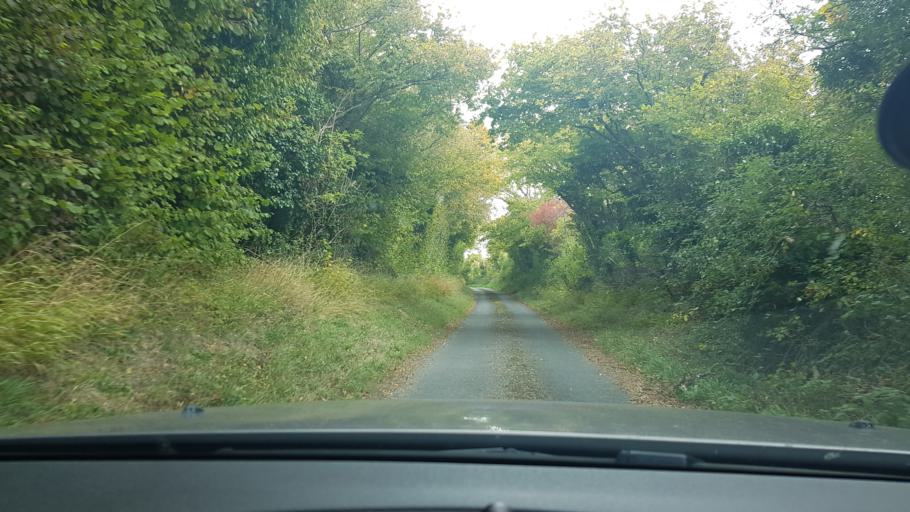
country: GB
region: England
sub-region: Wiltshire
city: Shalbourne
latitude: 51.3745
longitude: -1.5342
